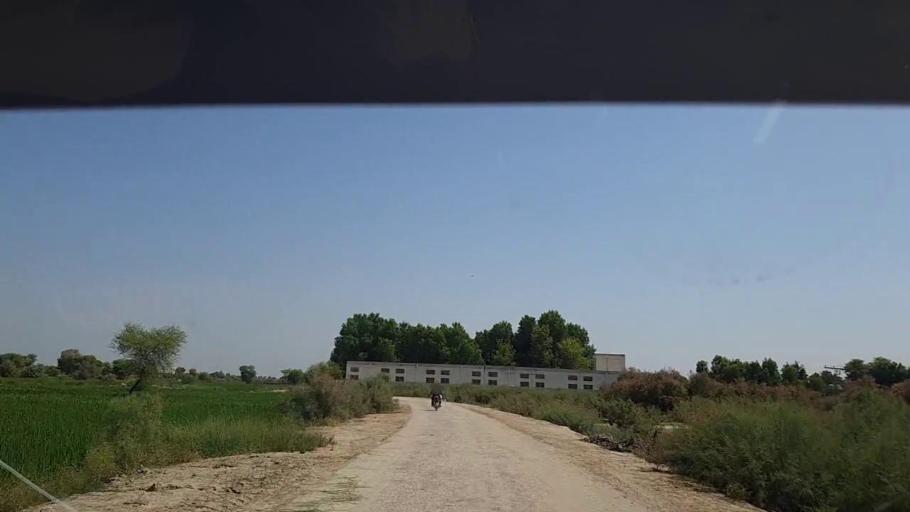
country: PK
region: Sindh
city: Kandhkot
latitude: 28.1651
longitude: 69.1610
